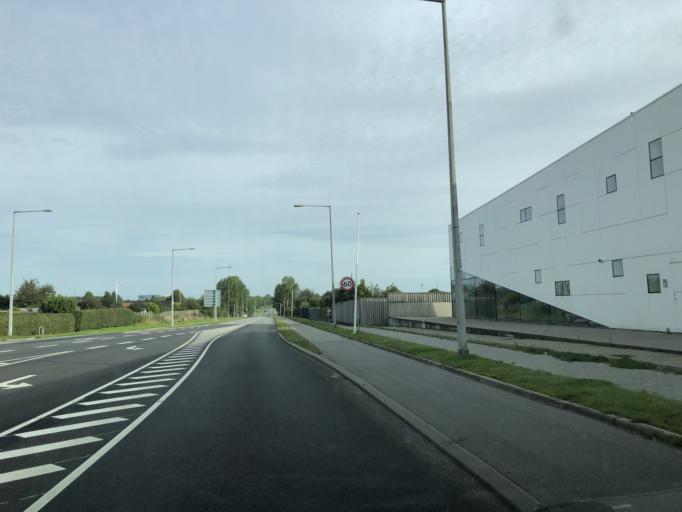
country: DK
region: South Denmark
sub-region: Fredericia Kommune
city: Fredericia
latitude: 55.5696
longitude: 9.7249
